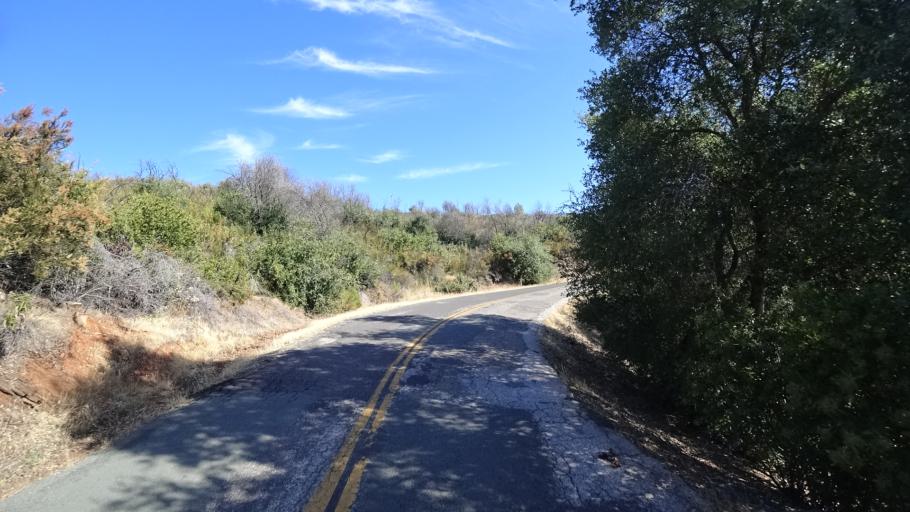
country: US
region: California
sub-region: Calaveras County
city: Mountain Ranch
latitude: 38.1700
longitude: -120.5421
